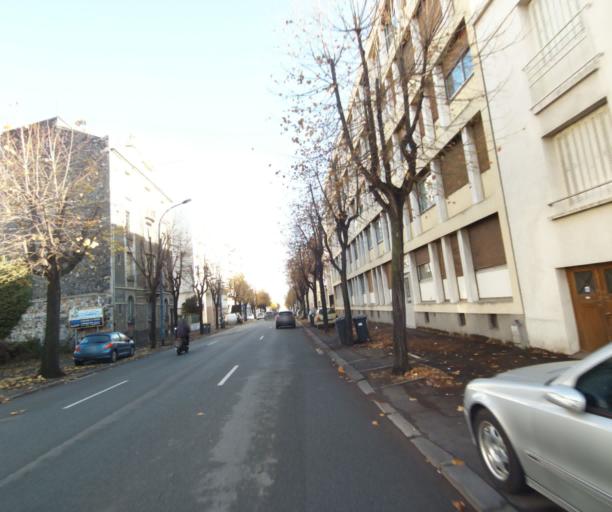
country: FR
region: Auvergne
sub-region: Departement du Puy-de-Dome
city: Clermont-Ferrand
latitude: 45.7695
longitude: 3.0911
